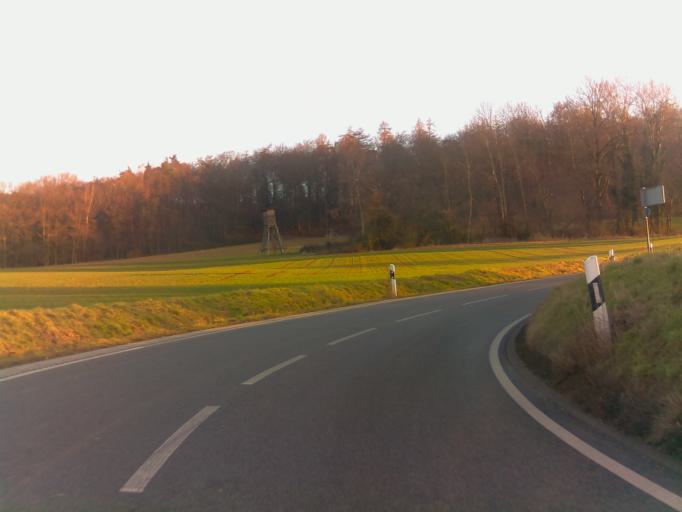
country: DE
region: Hesse
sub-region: Regierungsbezirk Darmstadt
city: Gelnhausen
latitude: 50.1623
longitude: 9.2053
